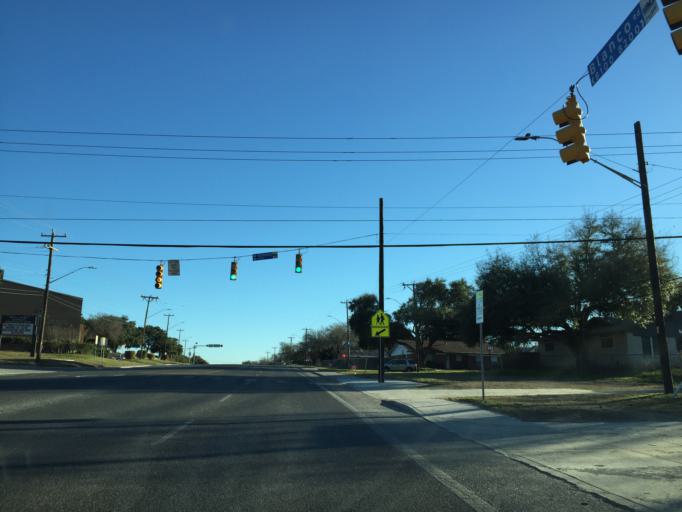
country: US
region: Texas
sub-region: Bexar County
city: Castle Hills
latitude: 29.5393
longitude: -98.5066
